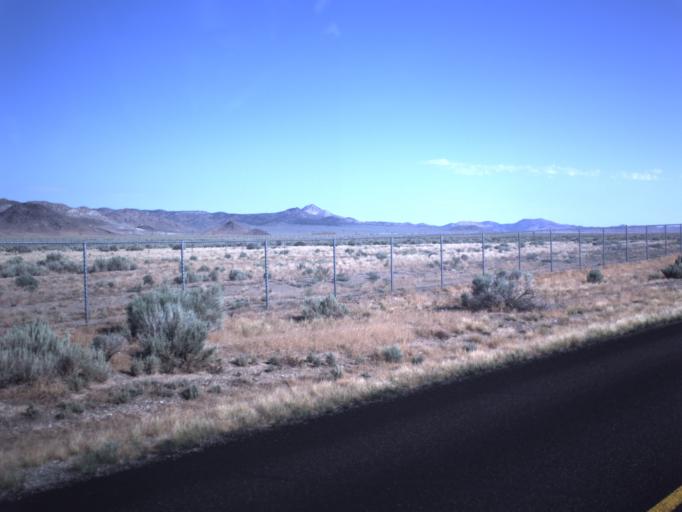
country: US
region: Utah
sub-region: Beaver County
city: Milford
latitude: 38.4321
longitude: -113.0097
